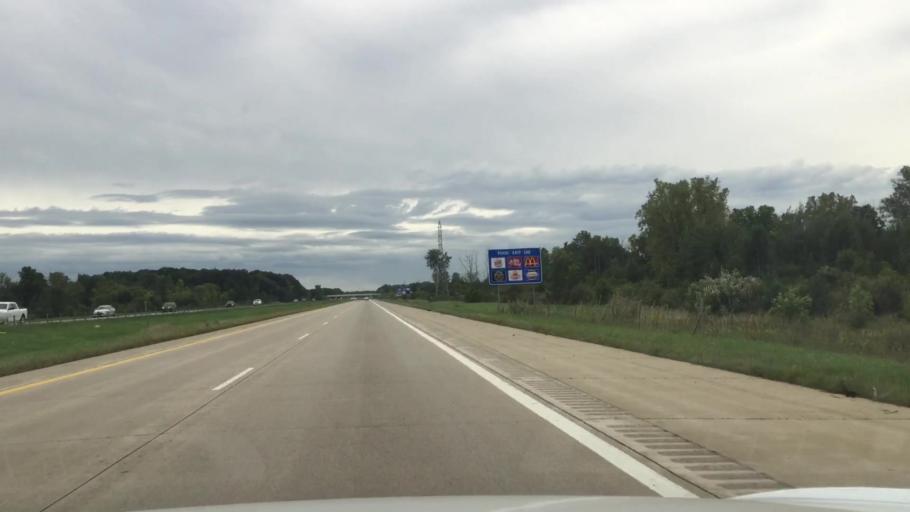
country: US
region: Michigan
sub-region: Saint Clair County
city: Marysville
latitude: 42.9310
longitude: -82.5071
